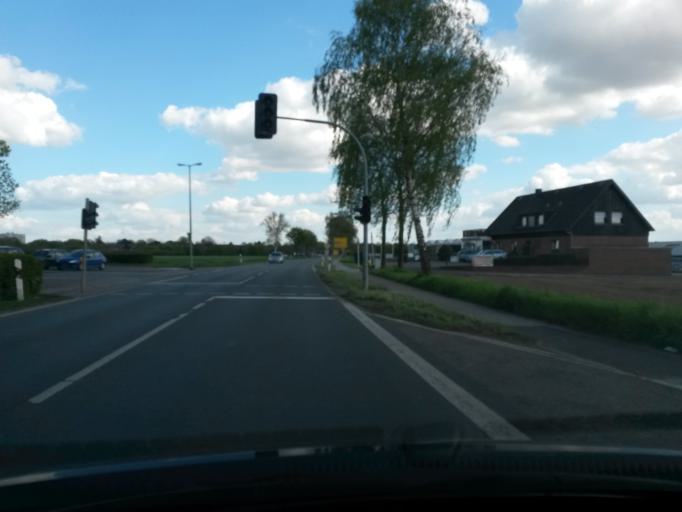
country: DE
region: North Rhine-Westphalia
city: Wegberg
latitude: 51.1601
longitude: 6.3506
